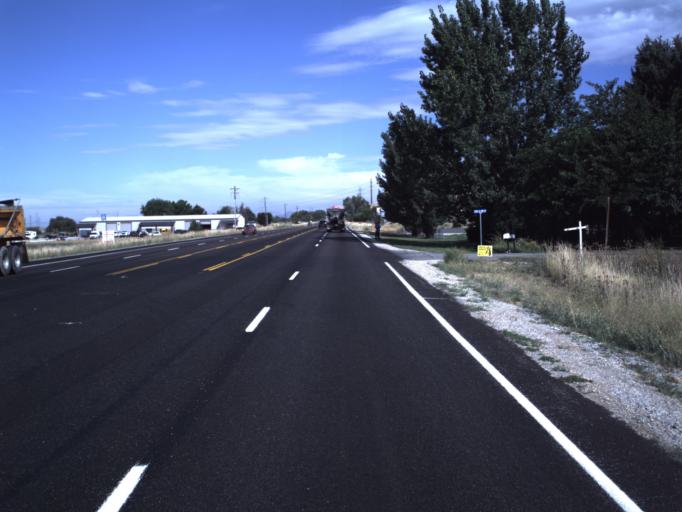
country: US
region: Utah
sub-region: Weber County
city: Pleasant View
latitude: 41.3246
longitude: -112.0191
